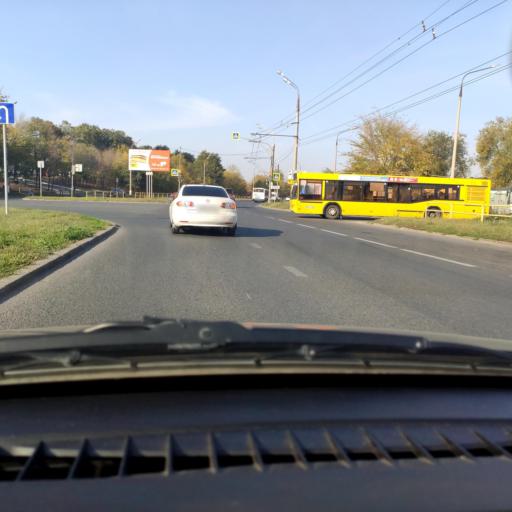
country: RU
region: Samara
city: Tol'yatti
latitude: 53.5062
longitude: 49.2549
